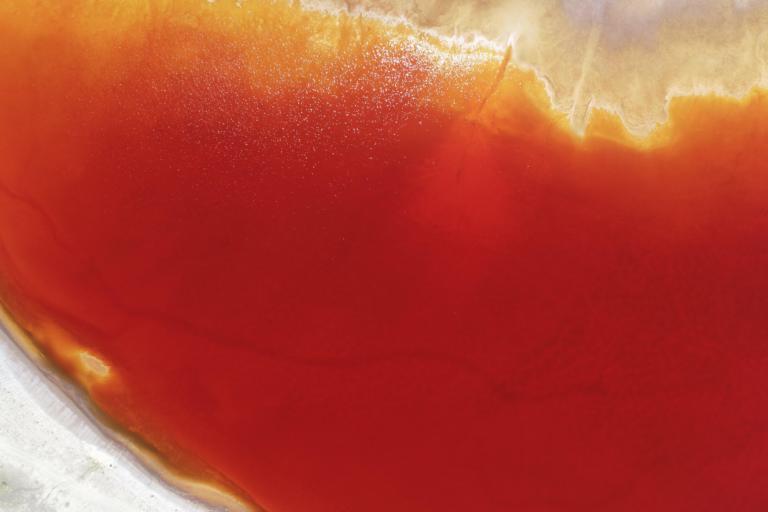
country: BO
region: La Paz
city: La Paz
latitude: -16.3423
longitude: -68.1609
